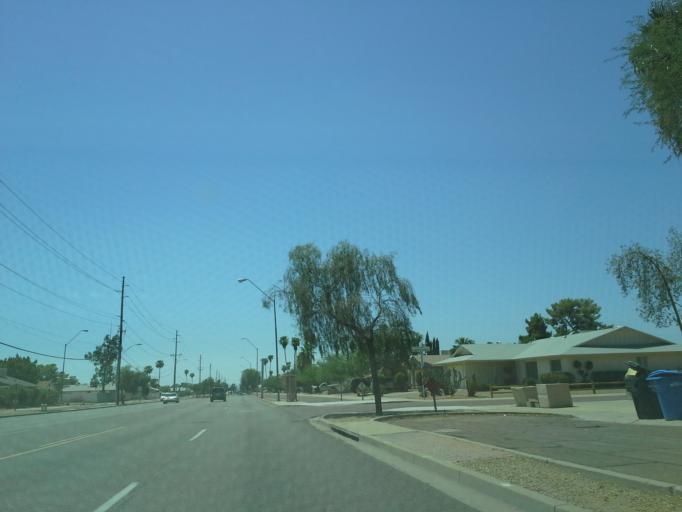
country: US
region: Arizona
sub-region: Maricopa County
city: Glendale
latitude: 33.6227
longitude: -112.1338
